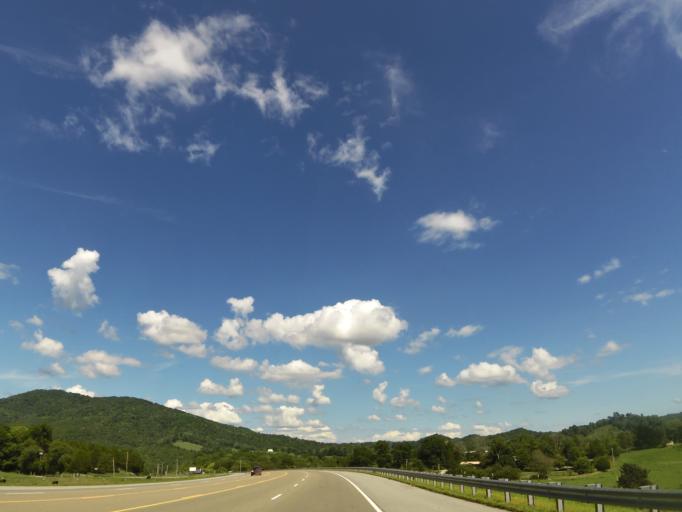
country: US
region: Tennessee
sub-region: Claiborne County
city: Tazewell
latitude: 36.4217
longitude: -83.5365
